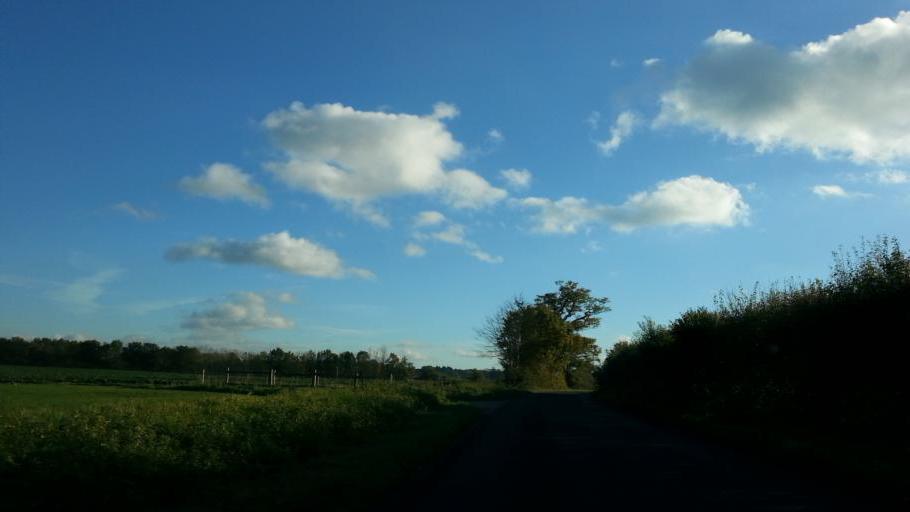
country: GB
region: England
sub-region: Suffolk
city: Thurston
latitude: 52.2388
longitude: 0.8076
